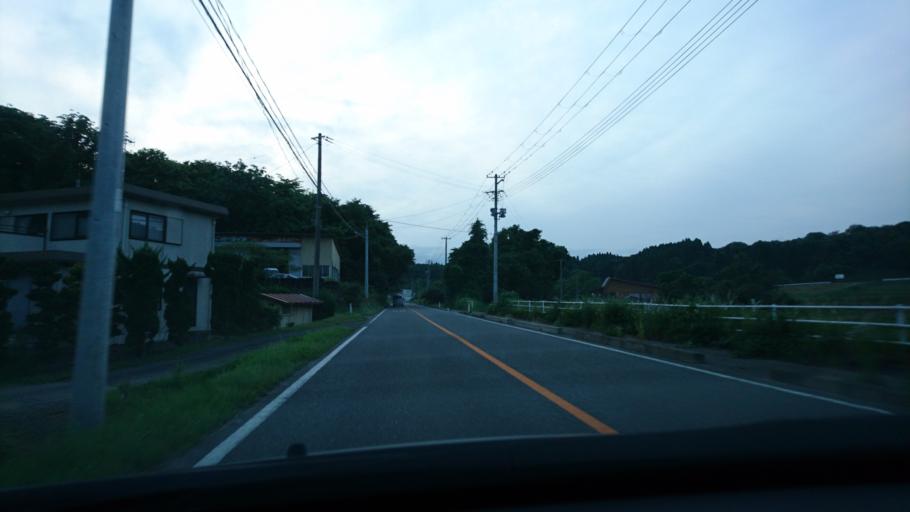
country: JP
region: Iwate
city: Ichinoseki
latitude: 38.7736
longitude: 140.9981
